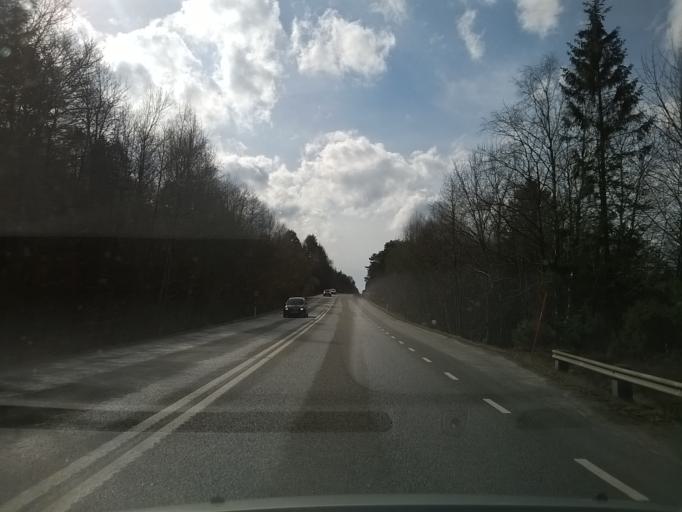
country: SE
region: Vaestra Goetaland
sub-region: Orust
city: Henan
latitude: 58.2646
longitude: 11.6837
